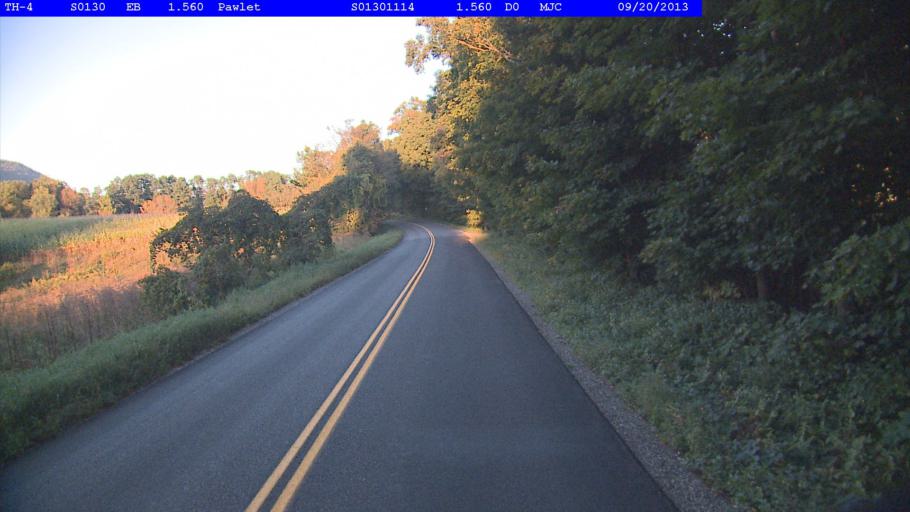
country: US
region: New York
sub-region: Washington County
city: Granville
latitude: 43.3582
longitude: -73.1238
